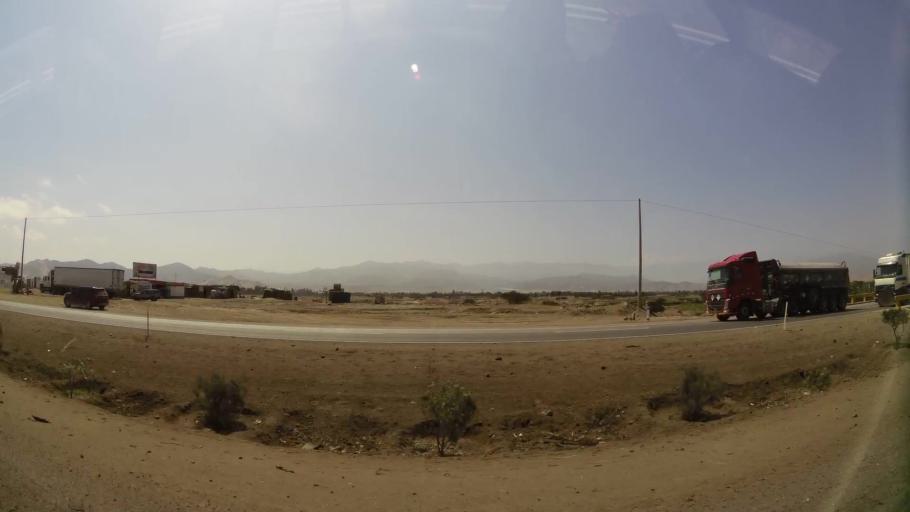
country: PE
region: Lima
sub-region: Provincia de Canete
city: Asia
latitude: -12.7910
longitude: -76.5639
